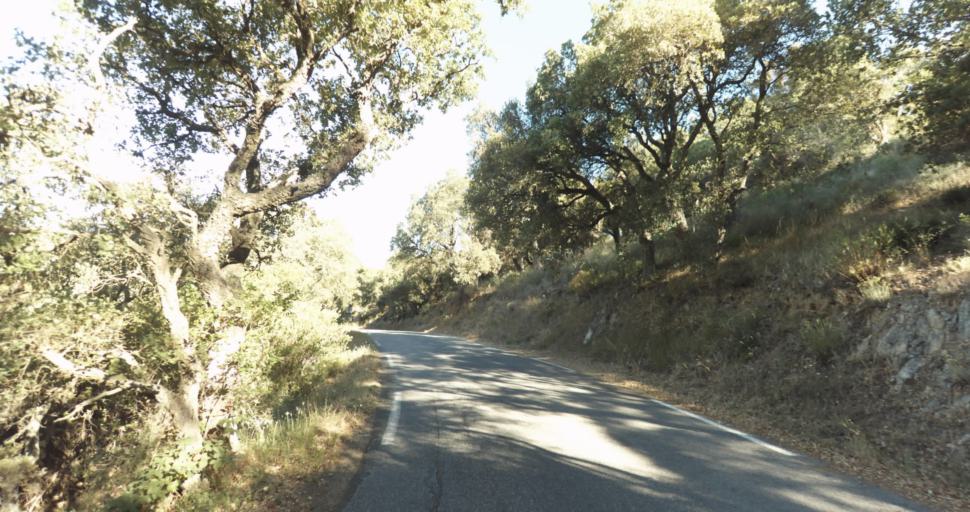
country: FR
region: Provence-Alpes-Cote d'Azur
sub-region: Departement du Var
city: Ramatuelle
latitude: 43.2152
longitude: 6.6038
